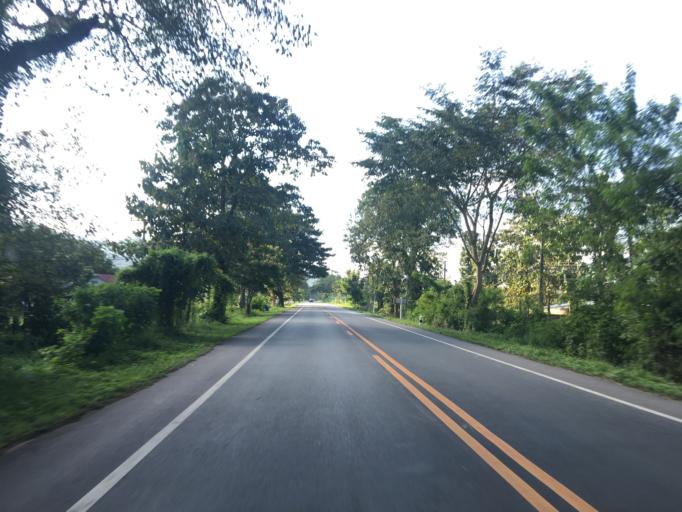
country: TH
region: Phayao
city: Chun
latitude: 19.3495
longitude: 100.1109
